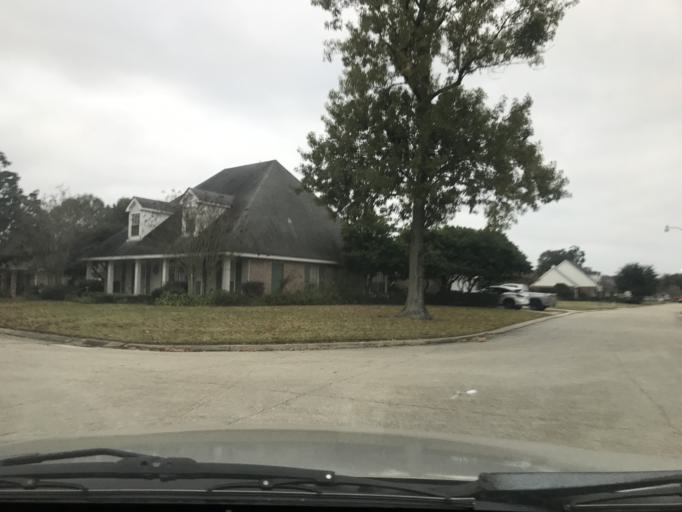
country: US
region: Louisiana
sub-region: Jefferson Parish
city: Woodmere
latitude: 29.8721
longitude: -90.0918
